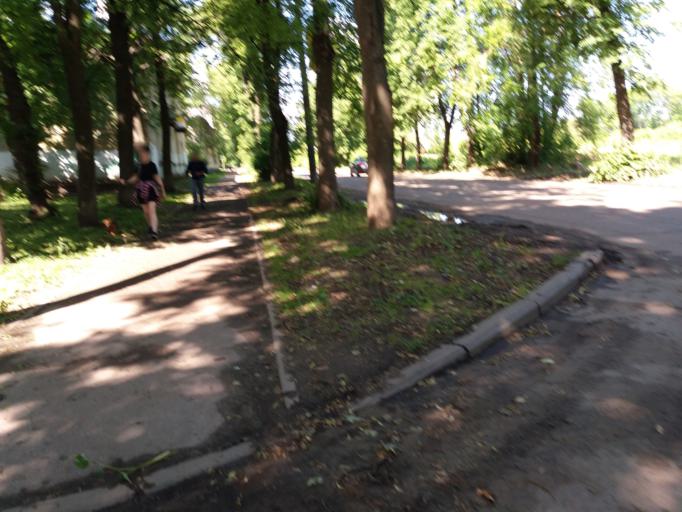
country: RU
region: Jaroslavl
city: Yaroslavl
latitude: 57.6427
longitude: 39.8326
